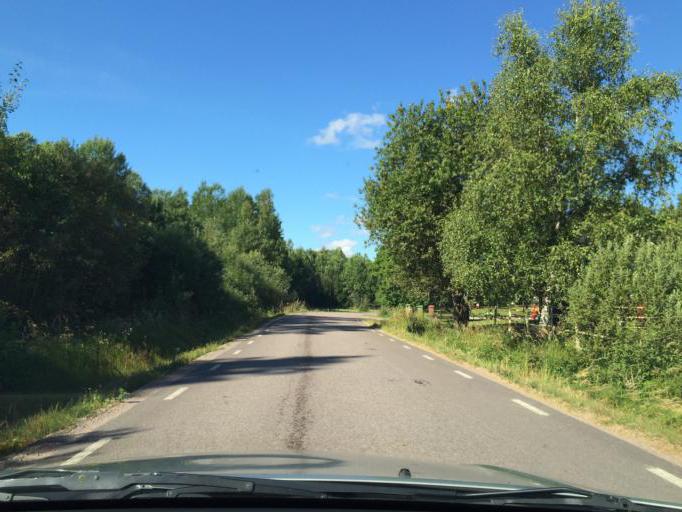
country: SE
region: Soedermanland
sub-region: Eskilstuna Kommun
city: Kvicksund
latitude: 59.4952
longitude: 16.3148
